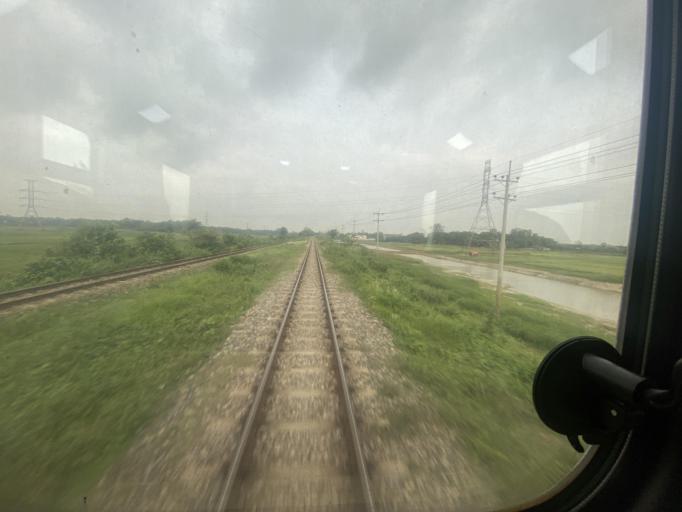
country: BD
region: Dhaka
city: Tungi
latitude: 23.9332
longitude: 90.5029
